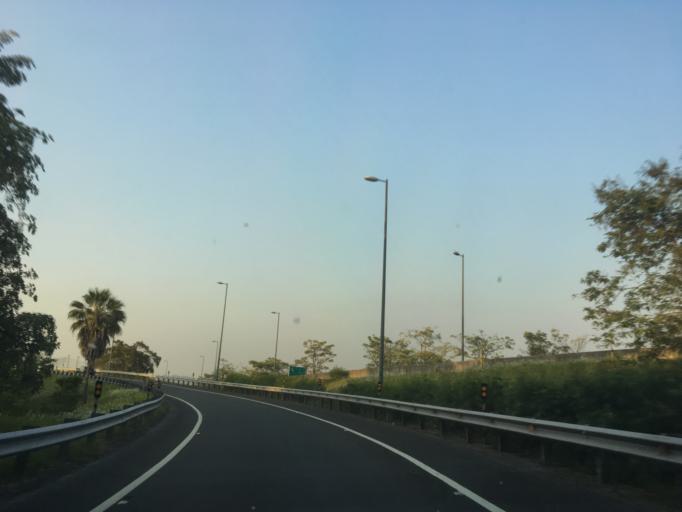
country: TW
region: Taiwan
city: Zhongxing New Village
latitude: 23.9472
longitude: 120.6699
